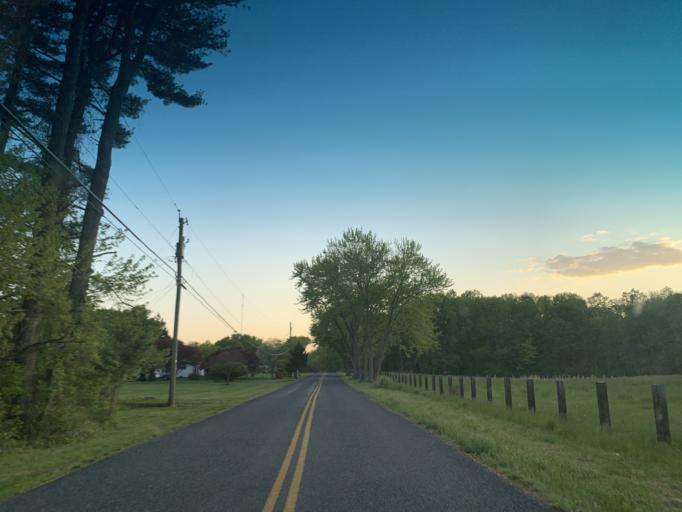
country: US
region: Maryland
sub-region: Harford County
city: Riverside
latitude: 39.5319
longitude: -76.2261
